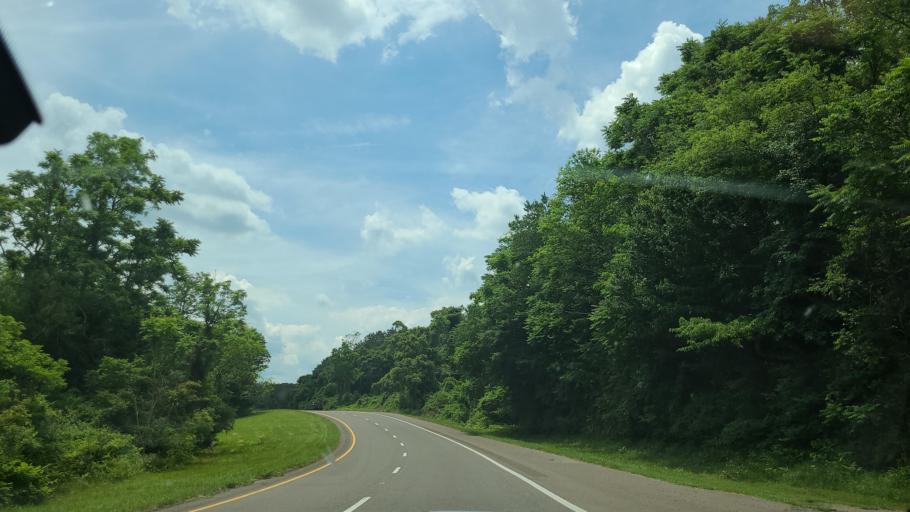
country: US
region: Georgia
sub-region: Fannin County
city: McCaysville
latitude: 35.0239
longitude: -84.3395
